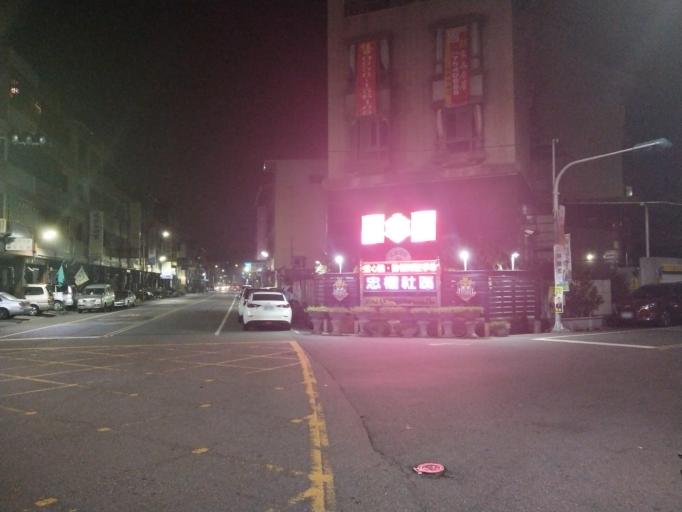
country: TW
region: Taiwan
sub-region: Changhua
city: Chang-hua
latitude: 24.0871
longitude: 120.5355
